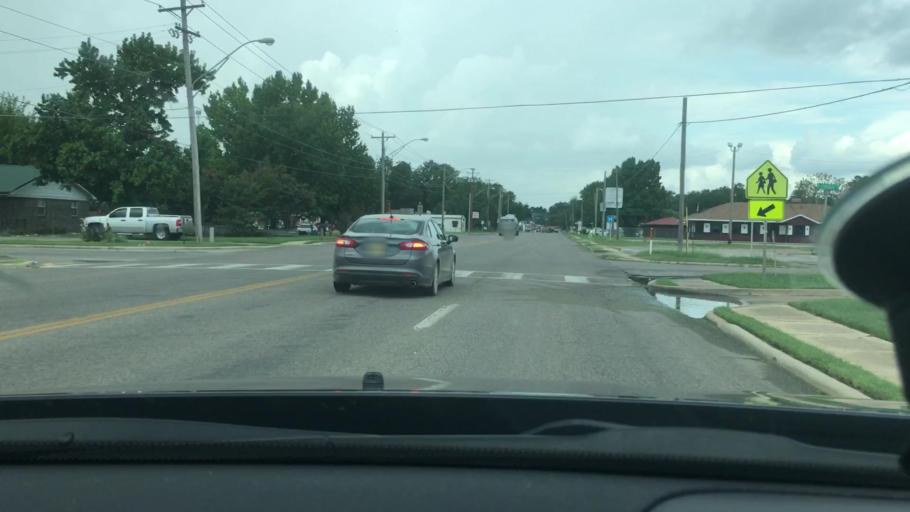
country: US
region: Oklahoma
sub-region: Johnston County
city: Tishomingo
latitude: 34.2306
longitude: -96.6620
